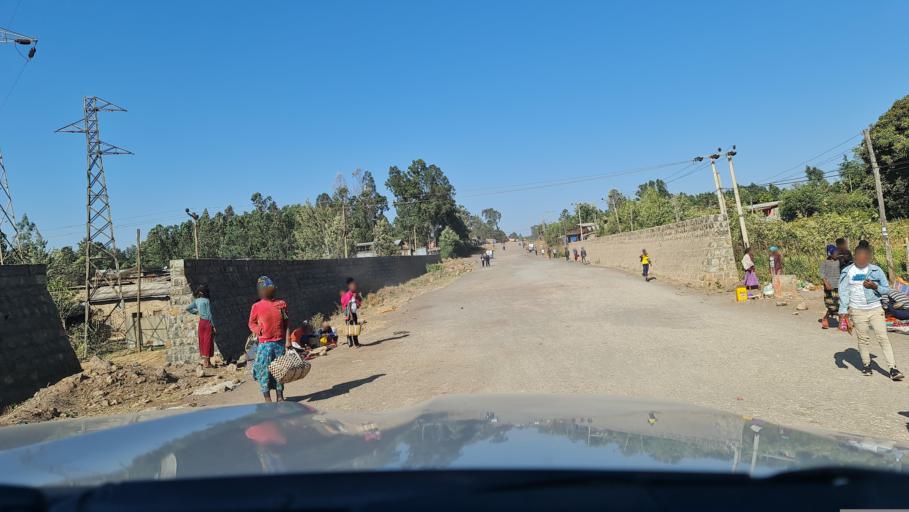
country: ET
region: Oromiya
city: Waliso
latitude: 8.5447
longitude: 37.9669
